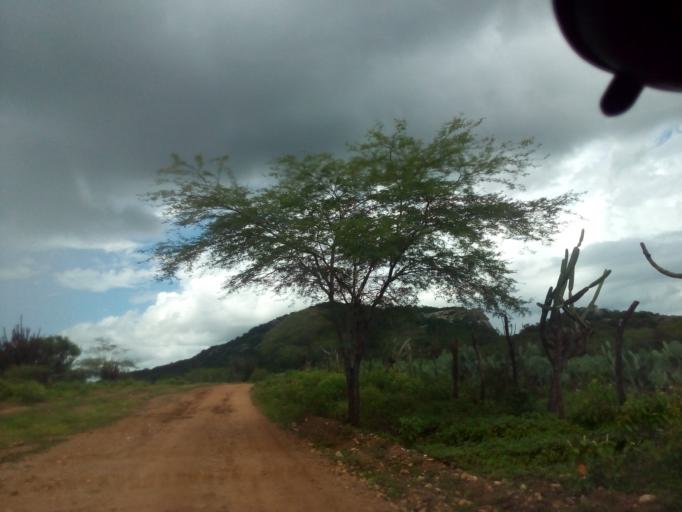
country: BR
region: Rio Grande do Norte
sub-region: Sao Paulo Do Potengi
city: Sao Paulo do Potengi
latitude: -5.9508
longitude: -35.9125
